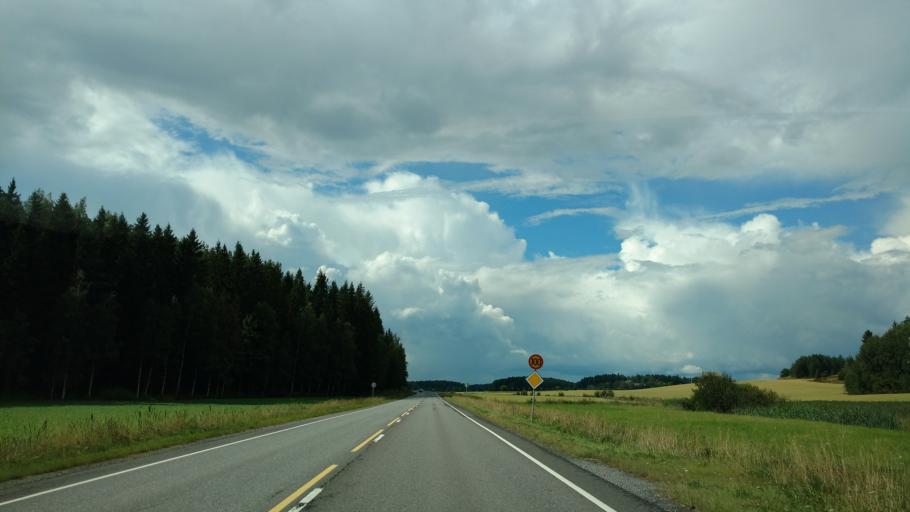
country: FI
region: Varsinais-Suomi
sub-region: Turku
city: Sauvo
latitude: 60.3866
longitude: 22.8828
